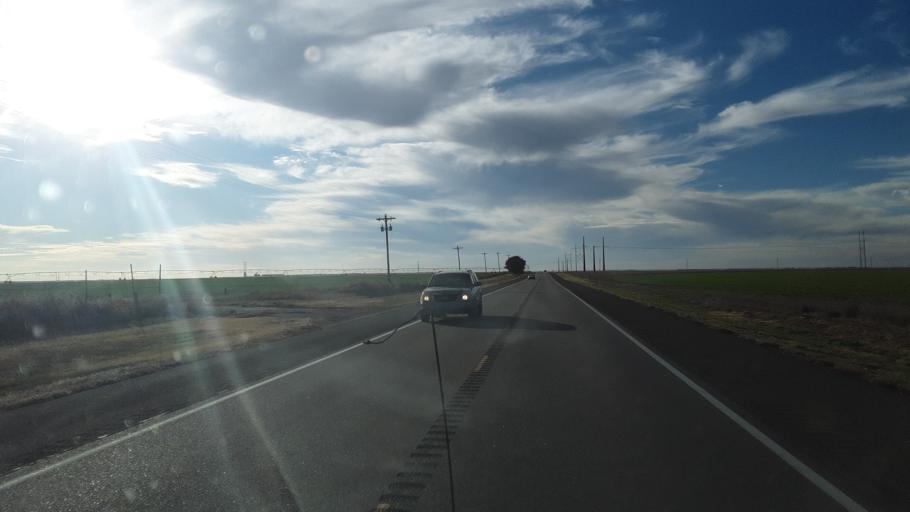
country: US
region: Kansas
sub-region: Finney County
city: Holcomb
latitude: 38.0034
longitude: -101.0598
